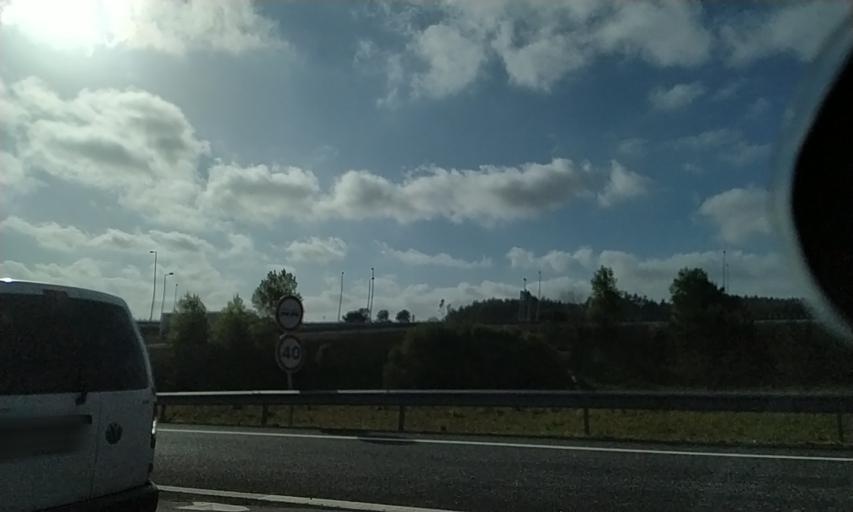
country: PT
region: Leiria
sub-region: Bombarral
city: Bombarral
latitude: 39.1958
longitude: -9.2000
